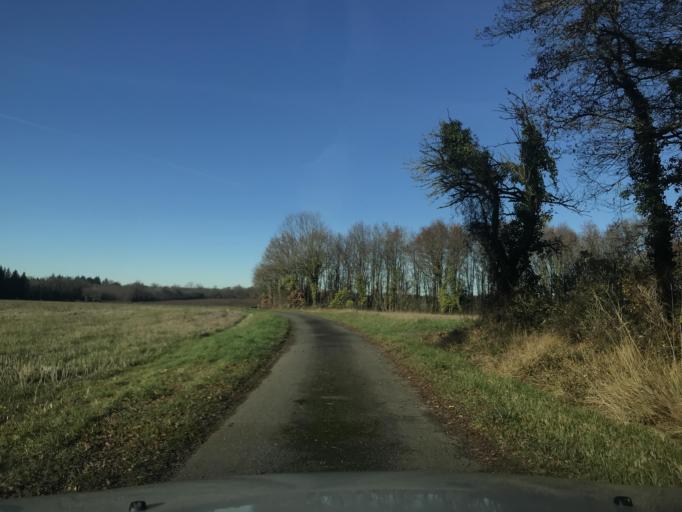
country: FR
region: Poitou-Charentes
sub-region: Departement de la Charente
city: Saint-Claud
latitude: 45.8511
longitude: 0.4920
